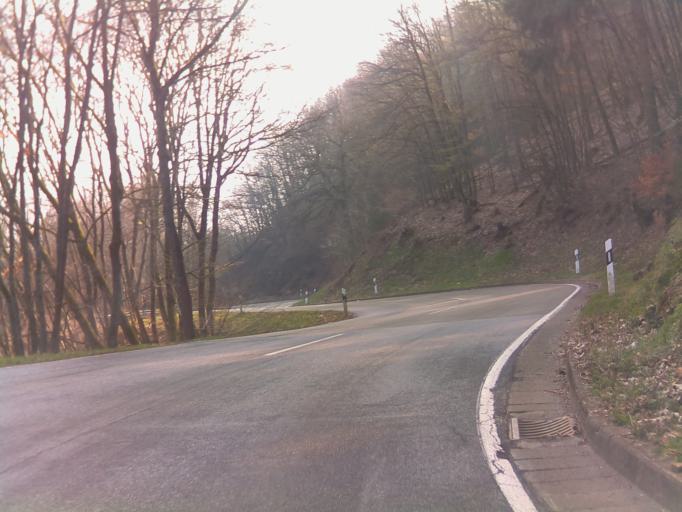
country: DE
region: Rheinland-Pfalz
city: Thallichtenberg
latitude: 49.5682
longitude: 7.3376
